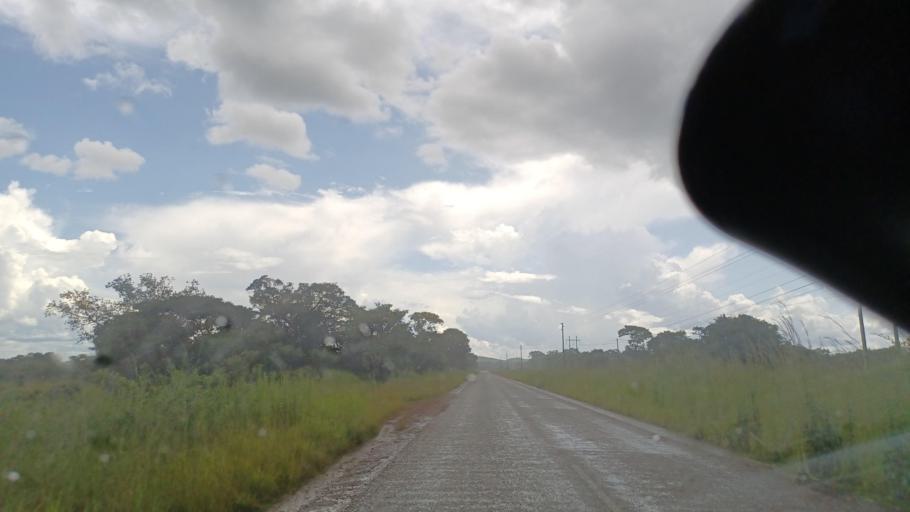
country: ZM
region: North-Western
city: Kasempa
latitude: -13.1023
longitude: 25.8893
